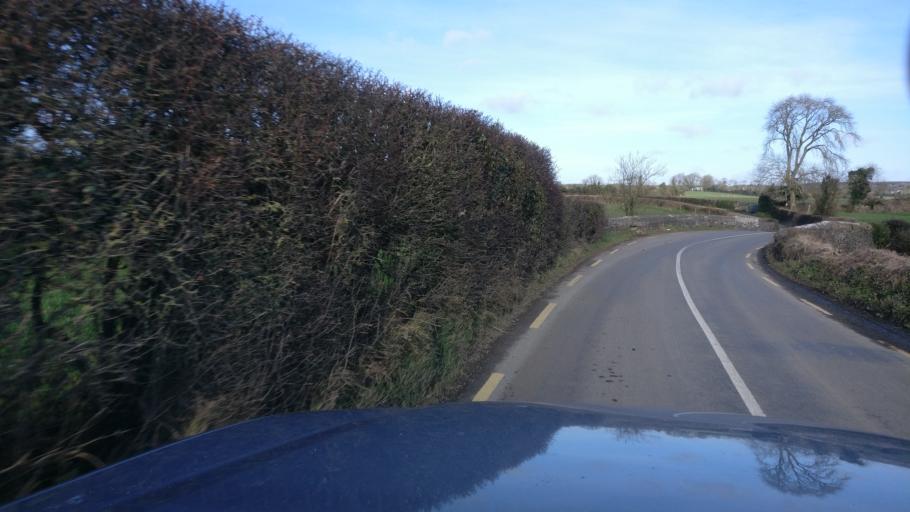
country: IE
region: Leinster
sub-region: Kilkenny
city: Castlecomer
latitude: 52.8743
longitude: -7.1625
